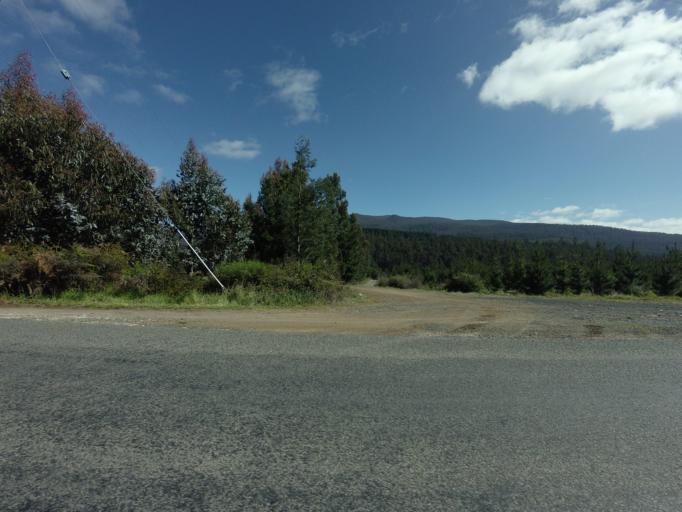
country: AU
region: Tasmania
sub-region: Derwent Valley
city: New Norfolk
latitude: -42.7471
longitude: 146.6497
